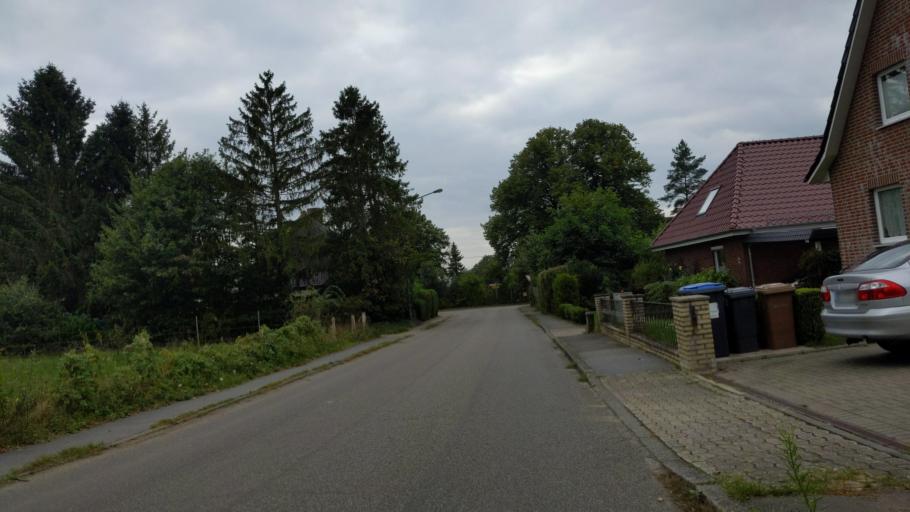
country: DE
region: Schleswig-Holstein
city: Klempau
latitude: 53.7879
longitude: 10.6790
